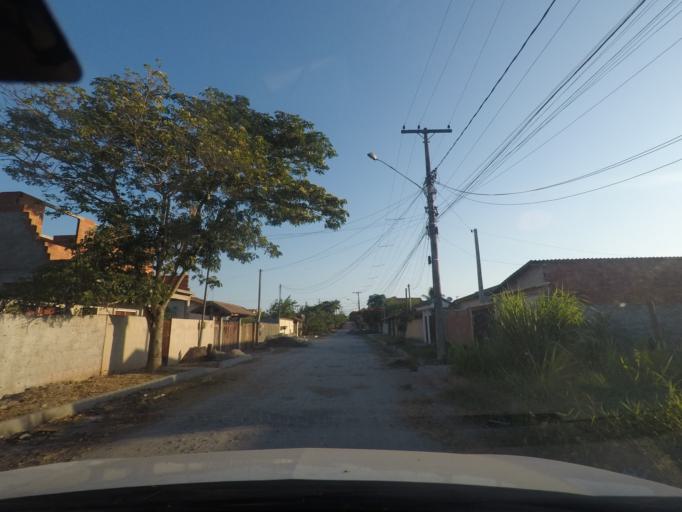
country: BR
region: Rio de Janeiro
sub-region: Marica
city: Marica
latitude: -22.9660
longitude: -42.9280
